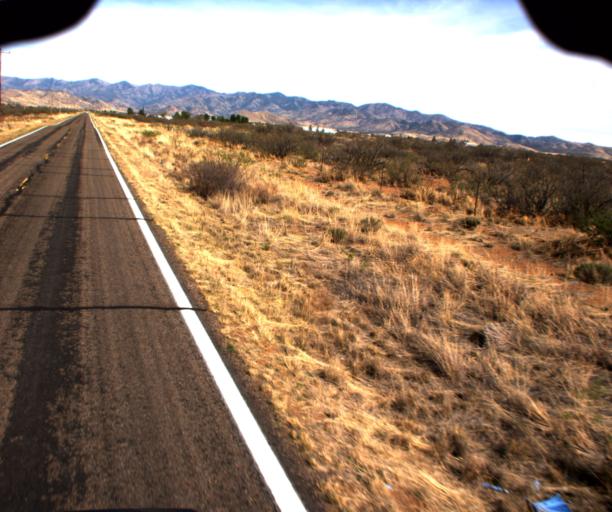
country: US
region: Arizona
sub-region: Cochise County
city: Willcox
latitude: 31.8760
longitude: -109.5094
